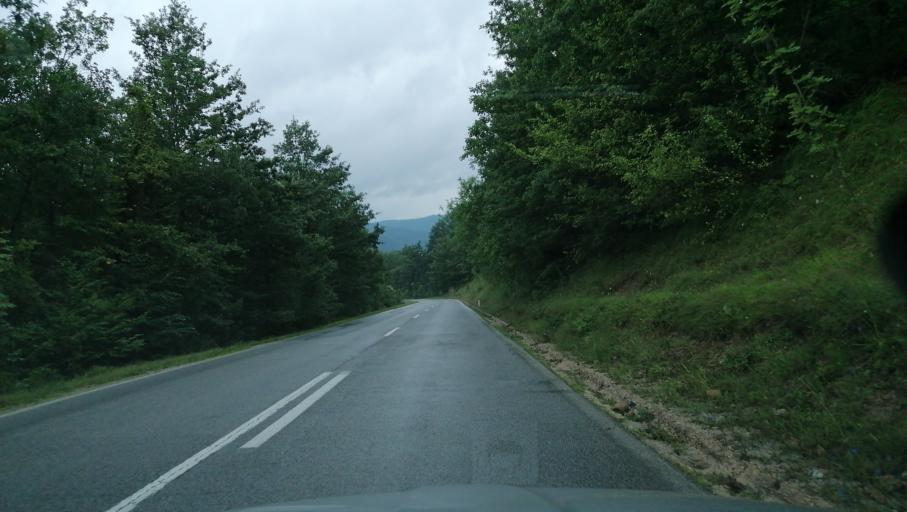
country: RS
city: Durici
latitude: 43.8074
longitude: 19.5104
